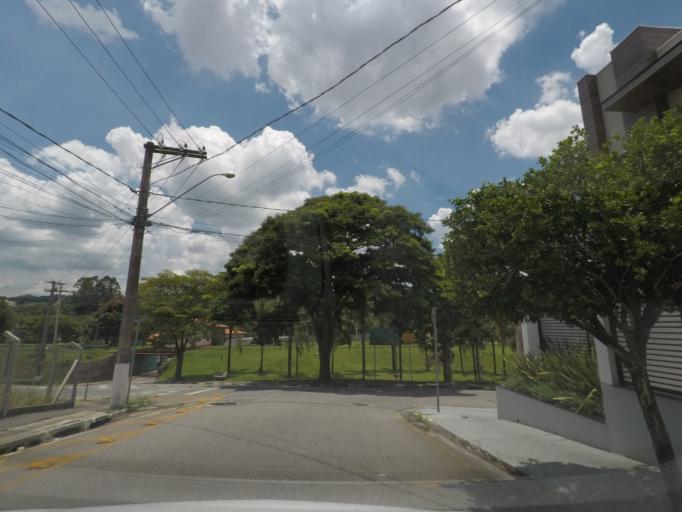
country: BR
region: Sao Paulo
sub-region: Vinhedo
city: Vinhedo
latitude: -23.0310
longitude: -46.9709
